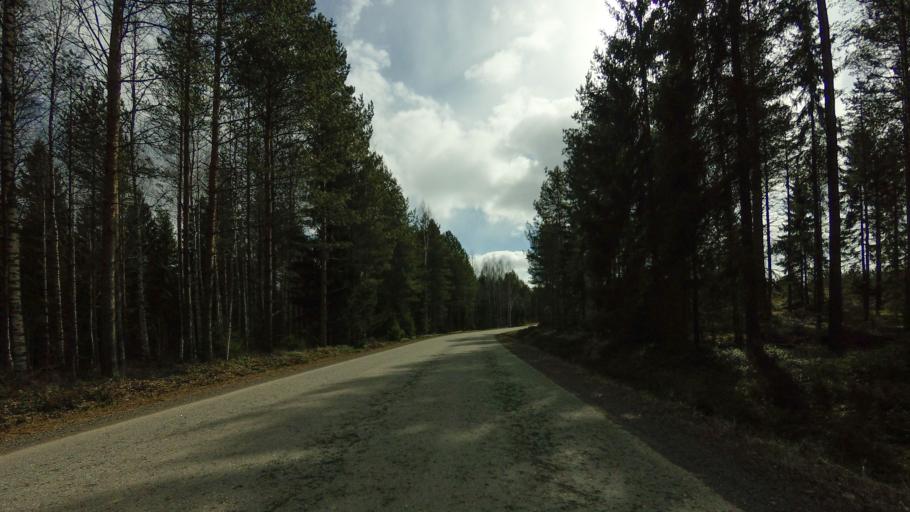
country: FI
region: Uusimaa
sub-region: Helsinki
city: Sammatti
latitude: 60.2791
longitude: 23.7755
